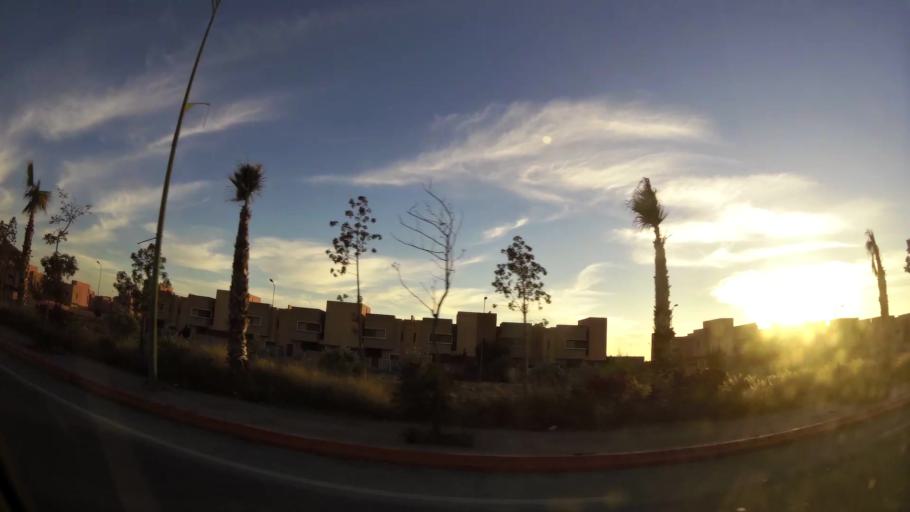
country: MA
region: Marrakech-Tensift-Al Haouz
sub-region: Marrakech
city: Marrakesh
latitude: 31.7632
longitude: -8.1173
